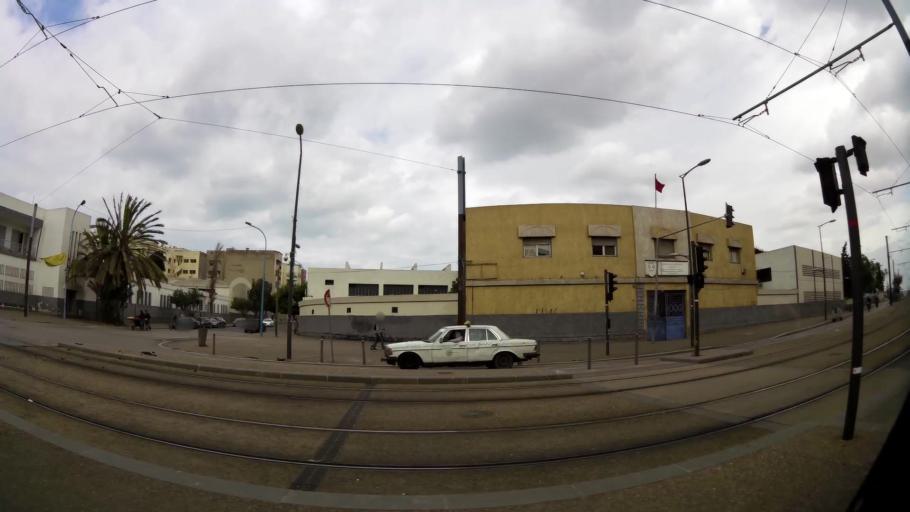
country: MA
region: Grand Casablanca
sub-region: Casablanca
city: Casablanca
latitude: 33.5902
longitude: -7.5749
